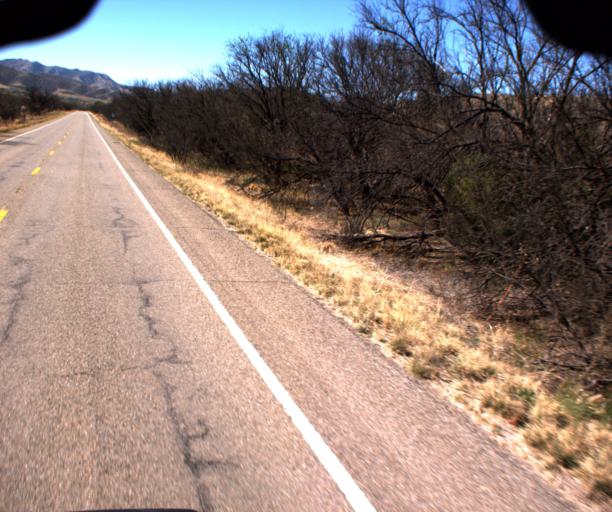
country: US
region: Arizona
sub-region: Santa Cruz County
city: Rio Rico
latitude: 31.5646
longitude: -110.7323
